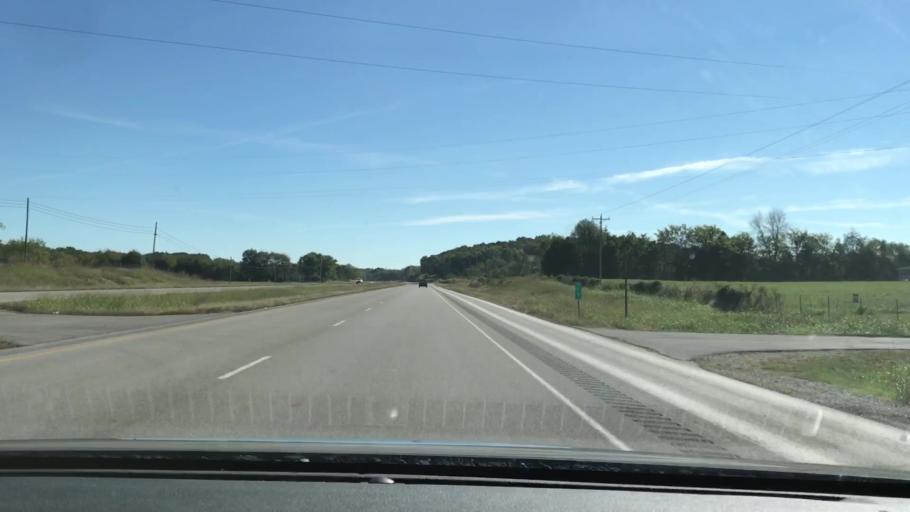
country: US
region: Kentucky
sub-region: Christian County
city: Hopkinsville
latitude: 36.8485
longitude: -87.3371
